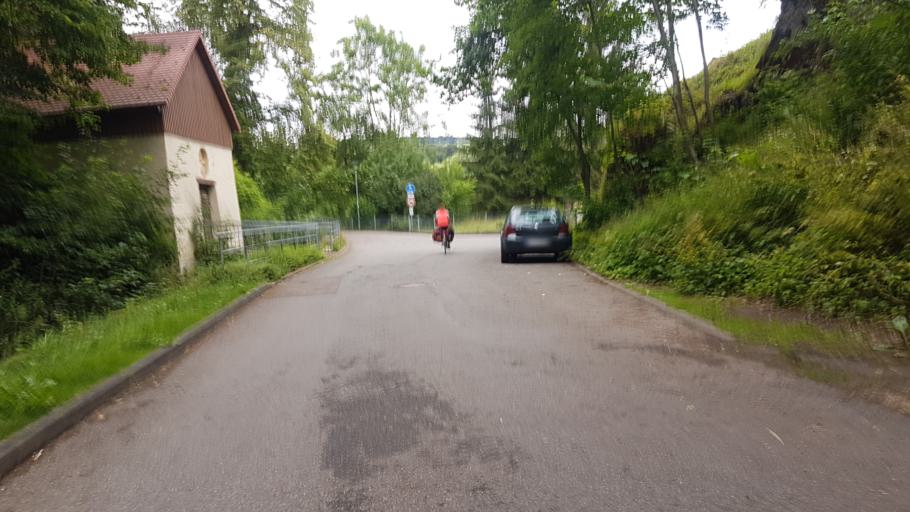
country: DE
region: Baden-Wuerttemberg
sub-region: Tuebingen Region
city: Obermarchtal
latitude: 48.2364
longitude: 9.5682
